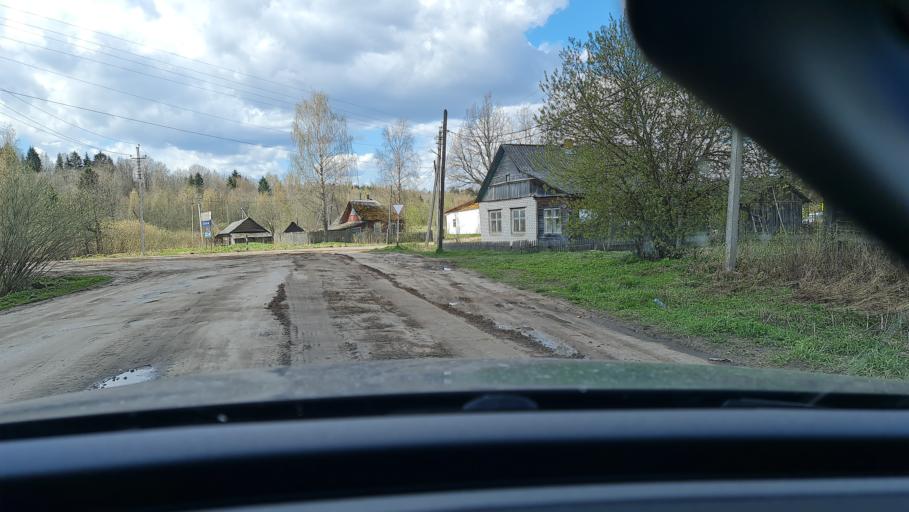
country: RU
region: Tverskaya
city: Toropets
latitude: 56.6439
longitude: 31.4211
